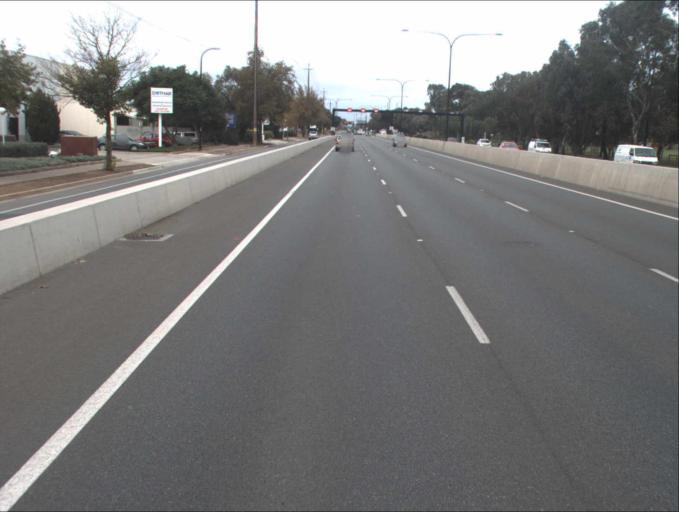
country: AU
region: South Australia
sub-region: Charles Sturt
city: Woodville
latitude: -34.8677
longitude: 138.5707
